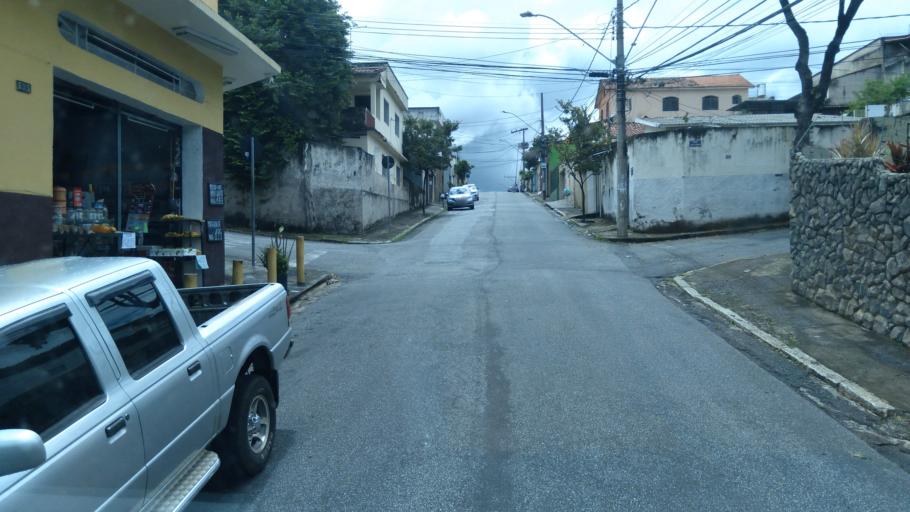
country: BR
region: Minas Gerais
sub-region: Belo Horizonte
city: Belo Horizonte
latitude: -19.9203
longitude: -43.9060
